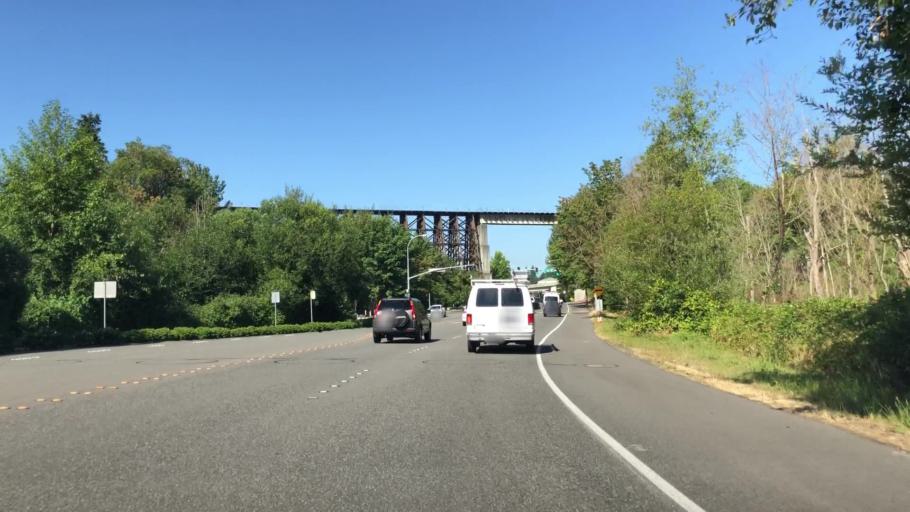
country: US
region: Washington
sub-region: King County
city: Bellevue
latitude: 47.6033
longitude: -122.1788
